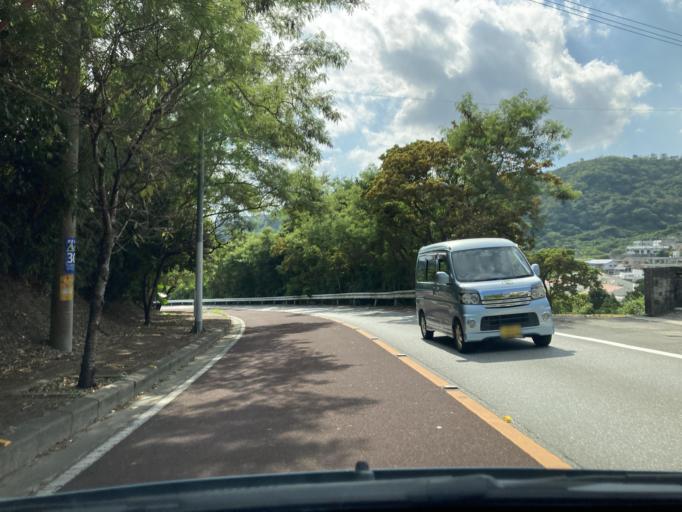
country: JP
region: Okinawa
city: Ginowan
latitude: 26.2580
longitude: 127.7844
